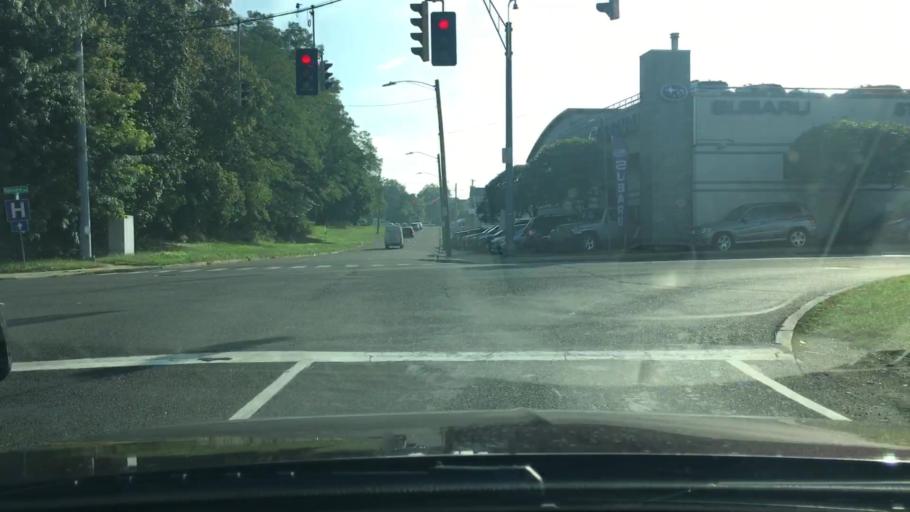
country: US
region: Connecticut
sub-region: Fairfield County
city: Riverside
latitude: 41.0443
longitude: -73.5611
